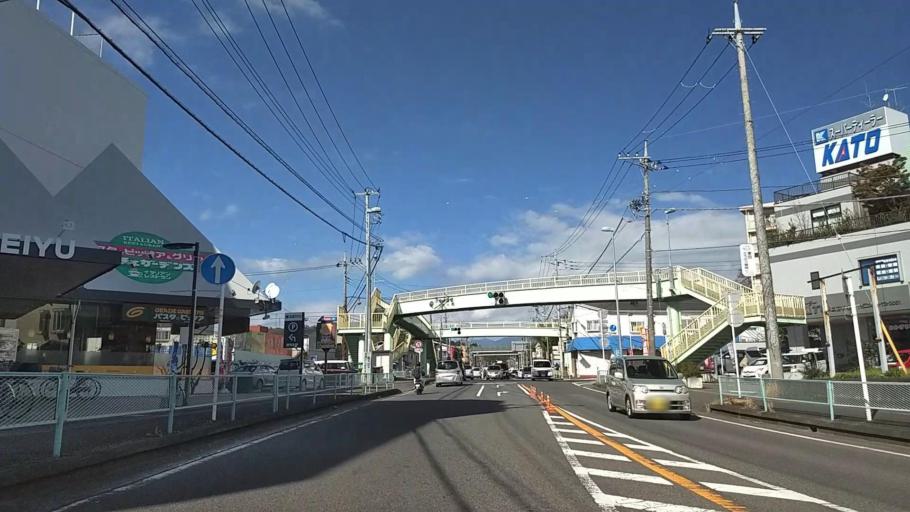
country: JP
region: Kanagawa
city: Ninomiya
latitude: 35.3091
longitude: 139.2476
